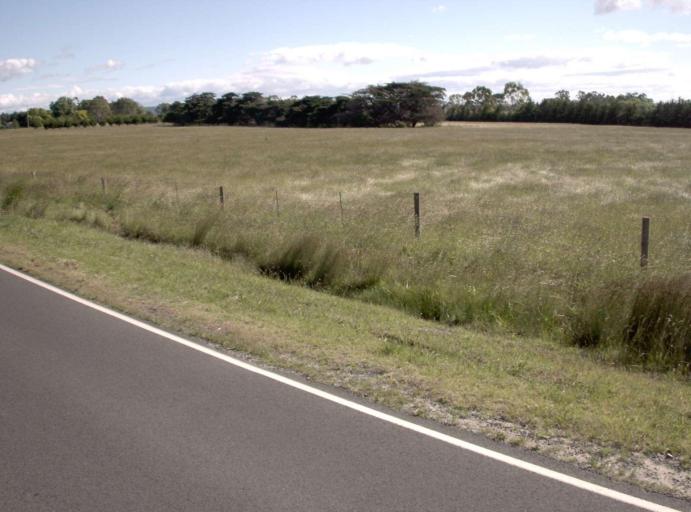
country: AU
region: Victoria
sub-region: Latrobe
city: Traralgon
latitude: -38.1817
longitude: 146.5002
